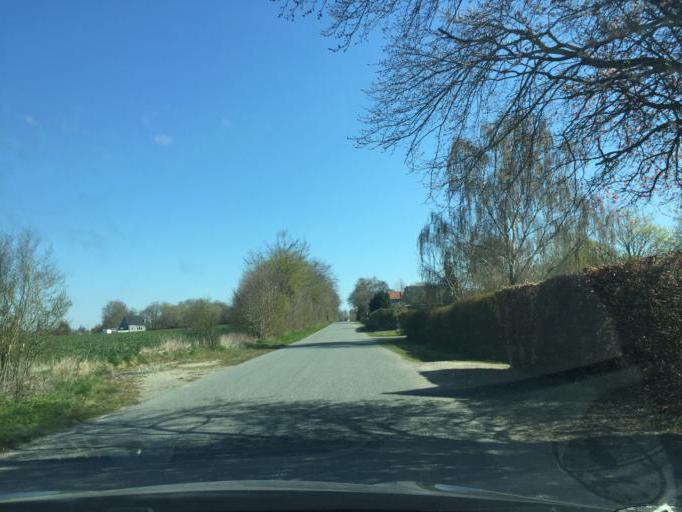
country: DK
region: South Denmark
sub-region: Faaborg-Midtfyn Kommune
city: Ringe
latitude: 55.2469
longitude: 10.4959
